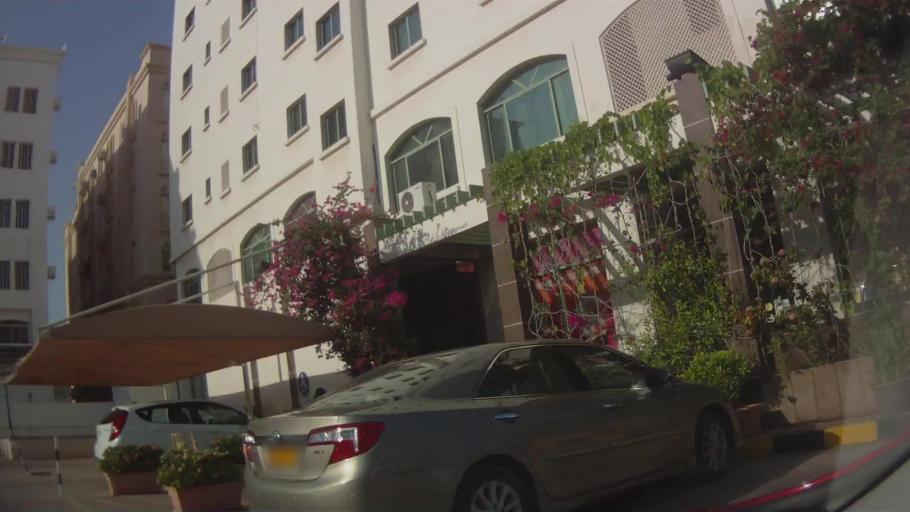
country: OM
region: Muhafazat Masqat
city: Bawshar
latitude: 23.5861
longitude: 58.4254
